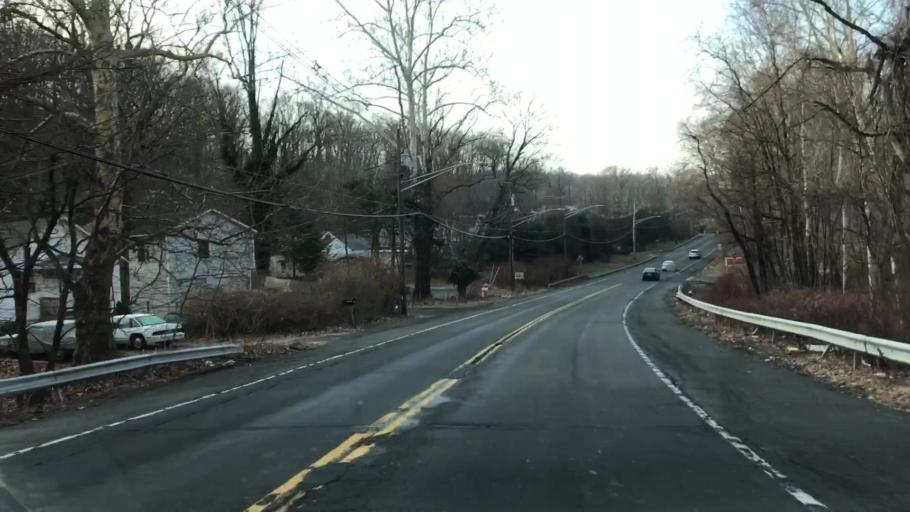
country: US
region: New York
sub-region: Rockland County
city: Valley Cottage
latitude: 41.1149
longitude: -73.9425
